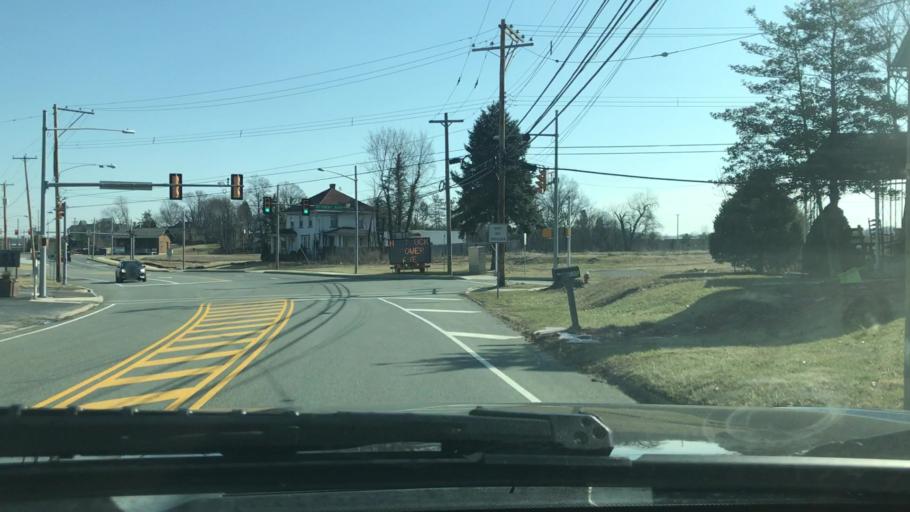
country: US
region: Pennsylvania
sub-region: Montgomery County
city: Audubon
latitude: 40.1330
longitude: -75.4569
